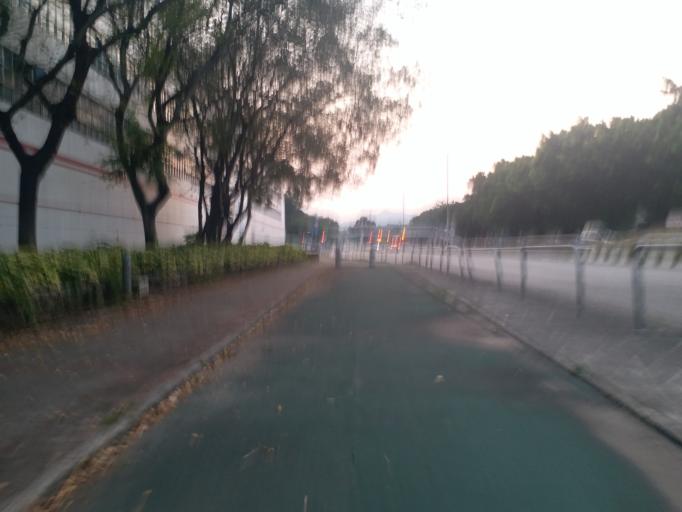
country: HK
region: Yuen Long
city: Yuen Long Kau Hui
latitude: 22.4412
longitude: 114.0096
